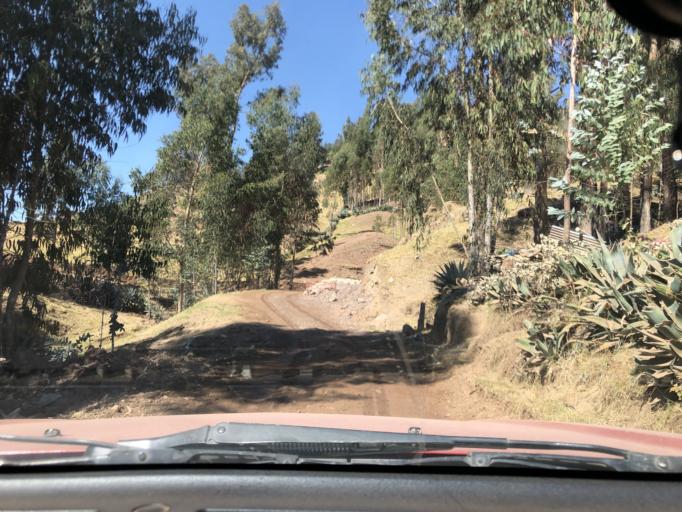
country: PE
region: Ayacucho
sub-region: Provincia de La Mar
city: Chilcas
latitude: -13.1694
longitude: -73.8505
